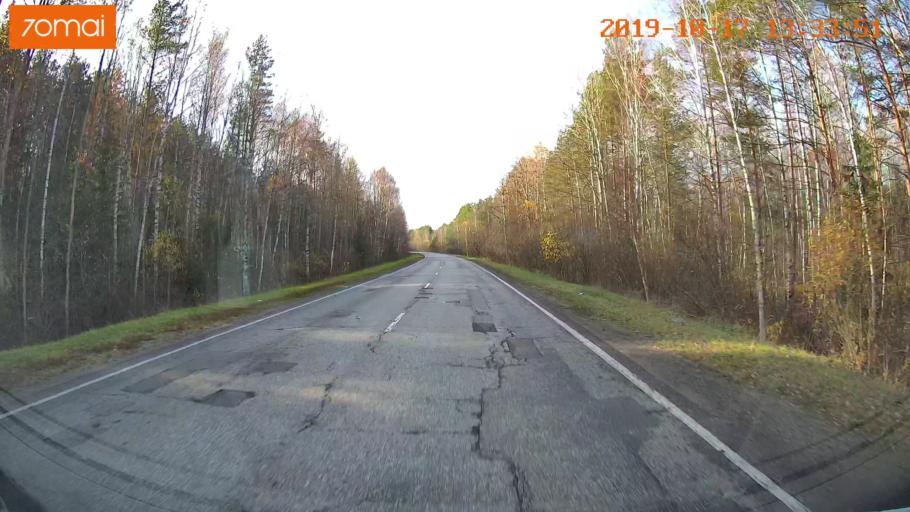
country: RU
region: Vladimir
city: Velikodvorskiy
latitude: 55.1443
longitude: 40.7314
